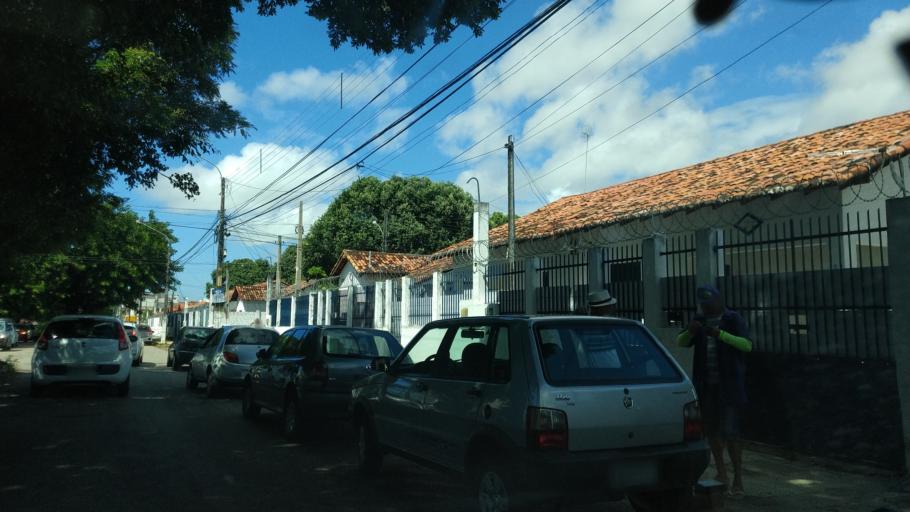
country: BR
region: Rio Grande do Norte
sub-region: Natal
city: Natal
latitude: -5.7990
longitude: -35.2189
